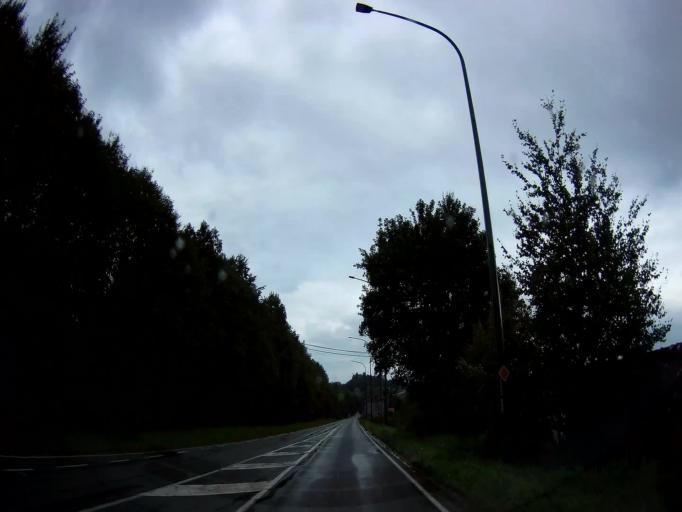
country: BE
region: Wallonia
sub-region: Province de Liege
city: Trooz
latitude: 50.5294
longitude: 5.7322
